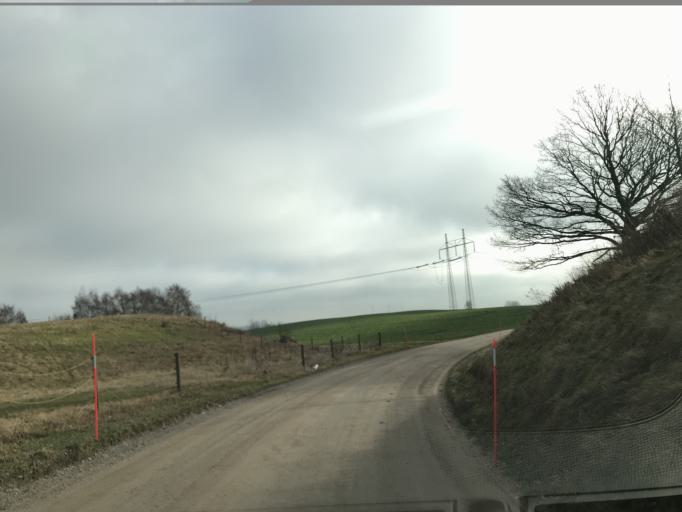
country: SE
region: Skane
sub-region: Svalovs Kommun
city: Teckomatorp
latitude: 55.8342
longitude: 13.0695
